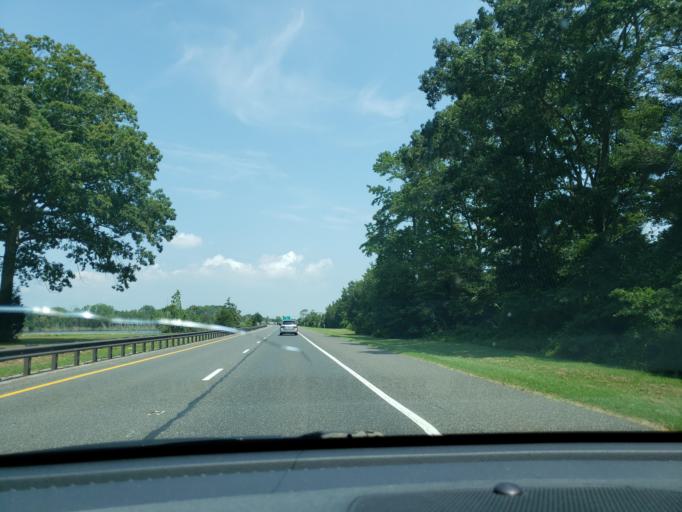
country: US
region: New Jersey
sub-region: Cape May County
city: Rio Grande
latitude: 39.0004
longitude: -74.8731
